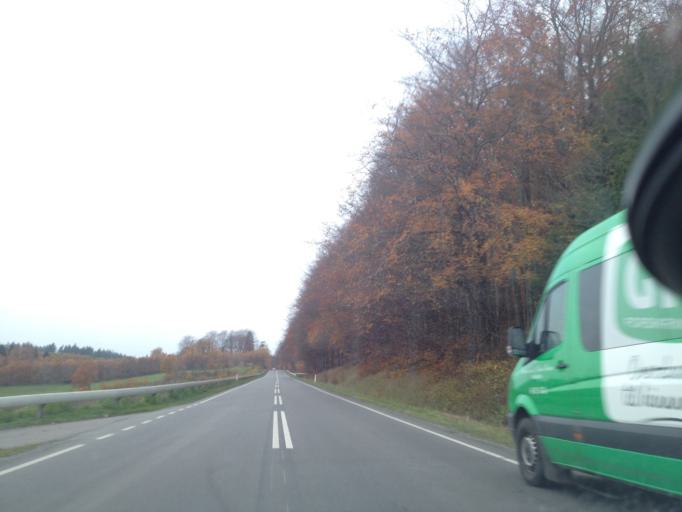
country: DK
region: South Denmark
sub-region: Nordfyns Kommune
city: Sonderso
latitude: 55.4379
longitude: 10.2226
